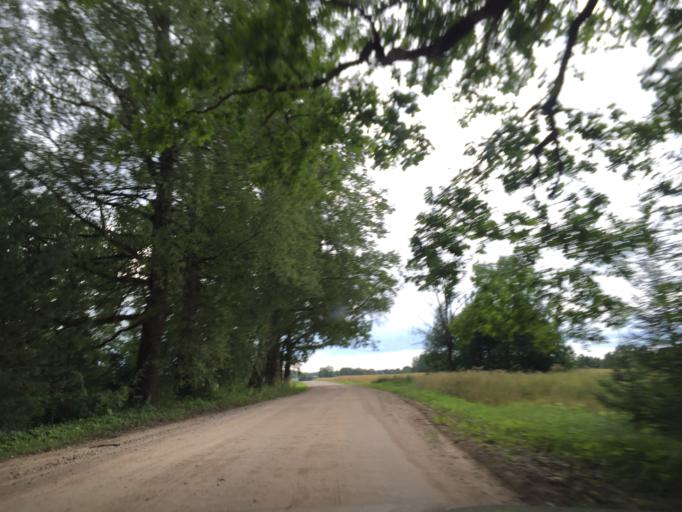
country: LV
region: Malpils
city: Malpils
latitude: 56.9473
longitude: 24.9973
